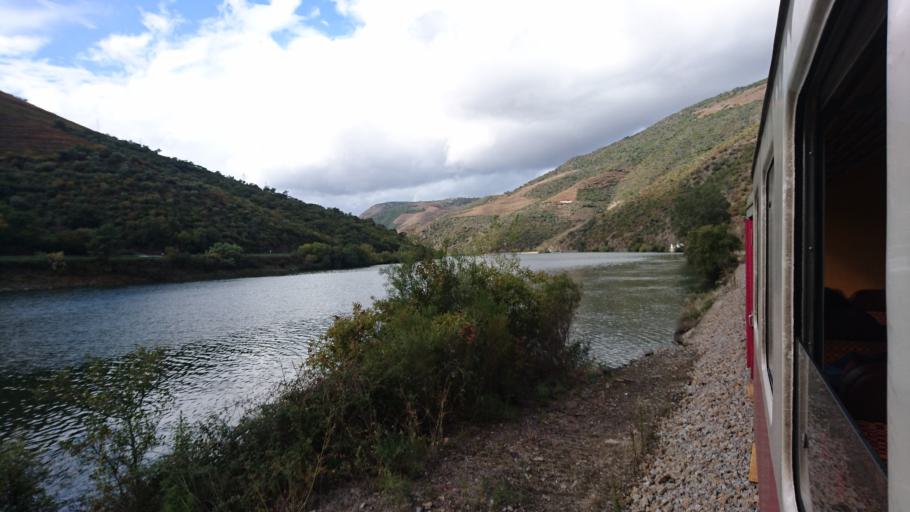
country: PT
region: Viseu
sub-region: Armamar
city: Armamar
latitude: 41.1627
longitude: -7.6534
